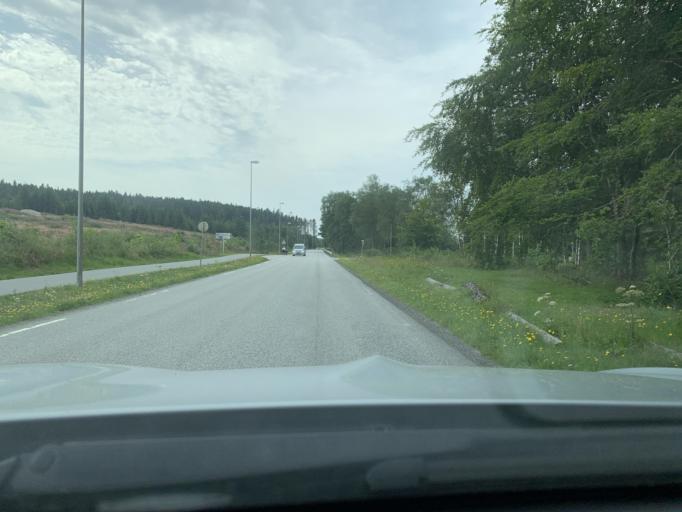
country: NO
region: Rogaland
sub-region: Time
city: Bryne
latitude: 58.7534
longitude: 5.6980
